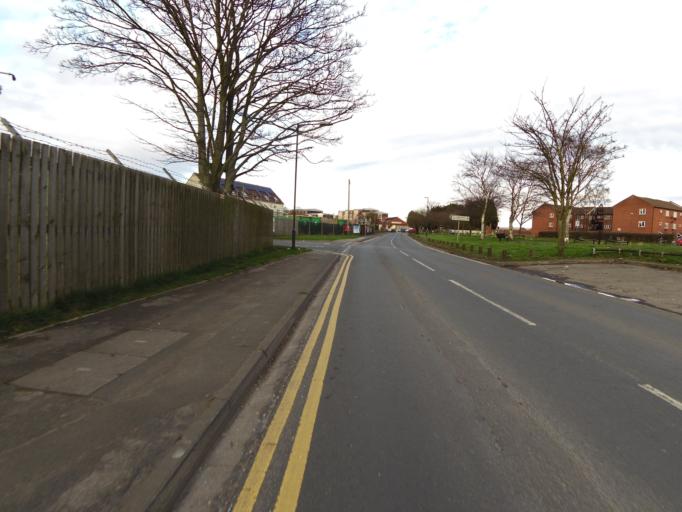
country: GB
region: England
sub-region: North Yorkshire
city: Selby
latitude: 53.7804
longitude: -1.0612
